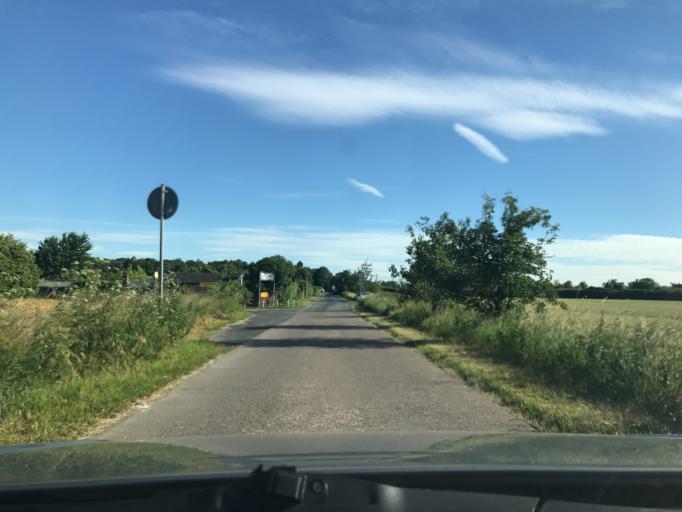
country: DE
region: Thuringia
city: Seebach
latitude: 51.1997
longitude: 10.4929
